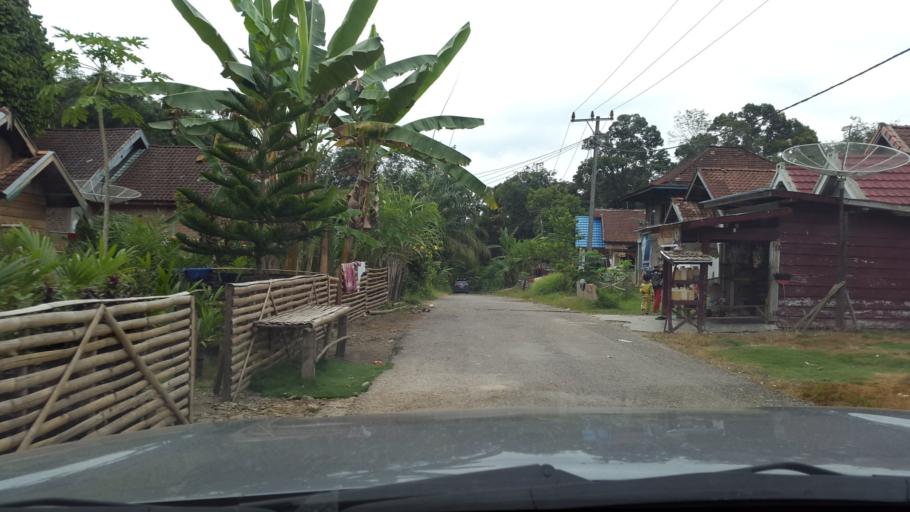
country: ID
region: South Sumatra
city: Terawas
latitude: -3.0263
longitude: 102.7353
